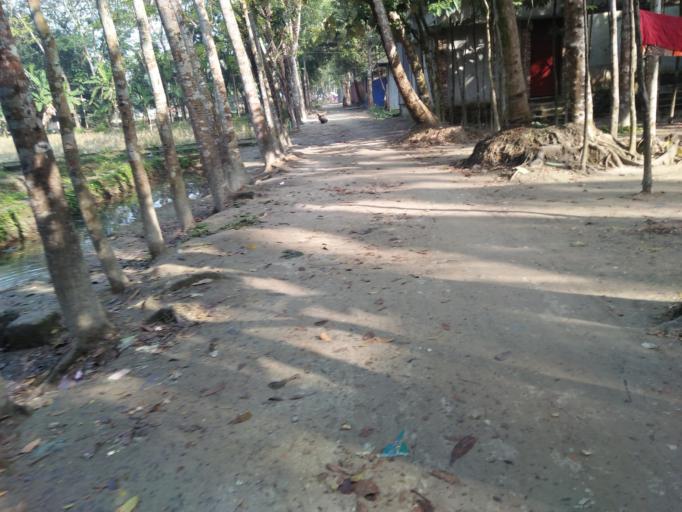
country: BD
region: Barisal
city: Bhola
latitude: 22.6774
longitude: 90.6400
